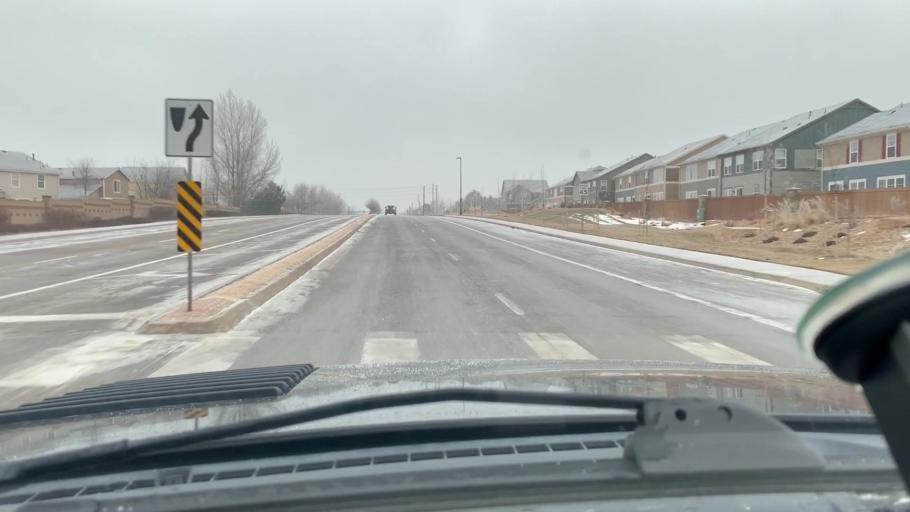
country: US
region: Colorado
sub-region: Arapahoe County
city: Dove Valley
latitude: 39.5679
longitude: -104.8028
